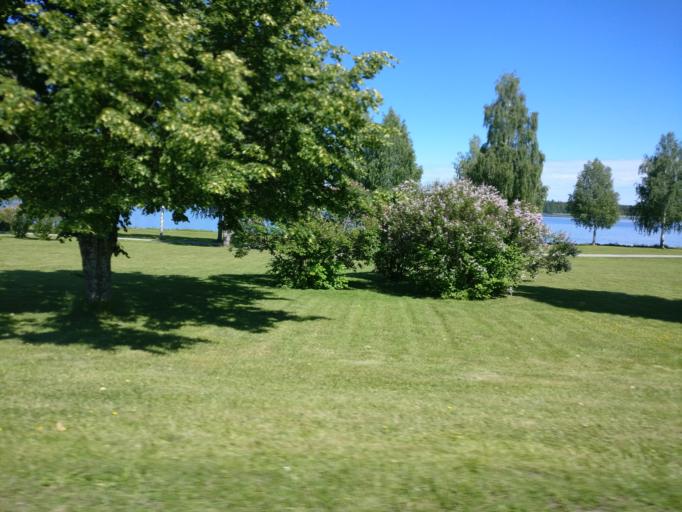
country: FI
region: Southern Savonia
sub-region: Savonlinna
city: Rantasalmi
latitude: 62.0674
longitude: 28.3022
